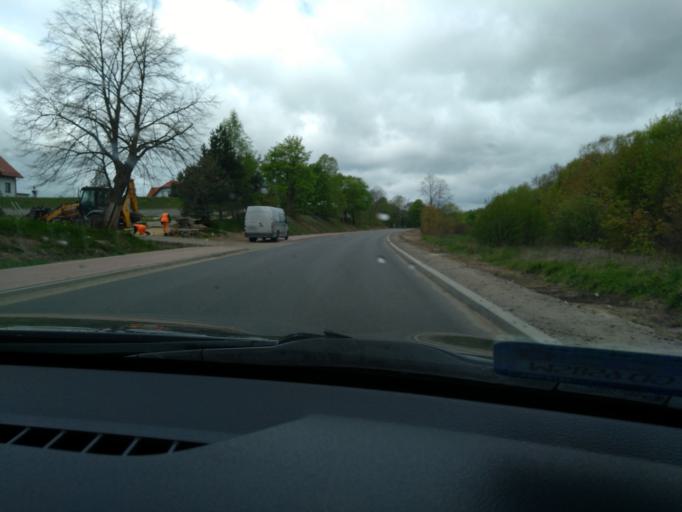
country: PL
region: Pomeranian Voivodeship
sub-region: Powiat kartuski
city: Garcz
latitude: 54.3466
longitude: 18.1259
